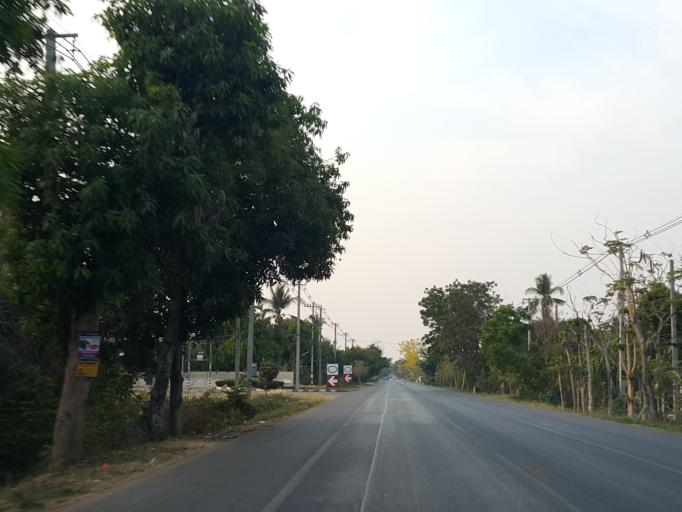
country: TH
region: Sukhothai
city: Si Samrong
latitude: 17.2349
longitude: 99.8582
